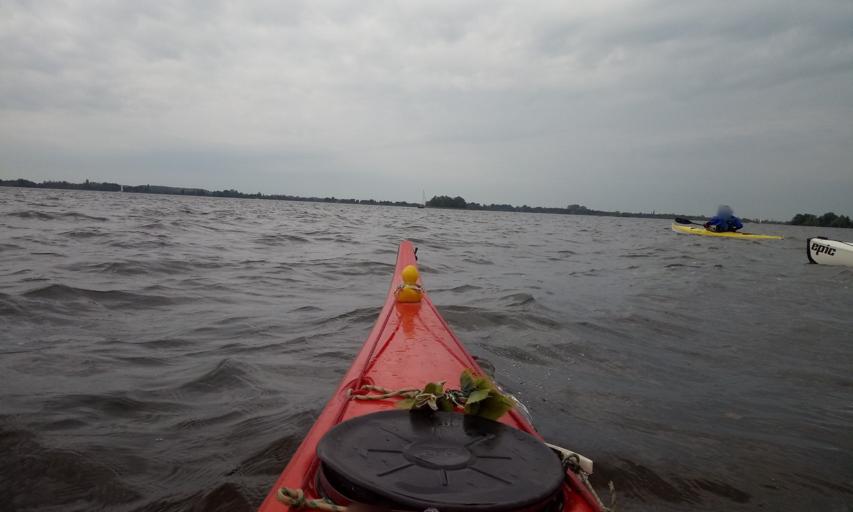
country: NL
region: North Holland
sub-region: Gemeente Wijdemeren
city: Oud-Loosdrecht
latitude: 52.1833
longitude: 5.0662
